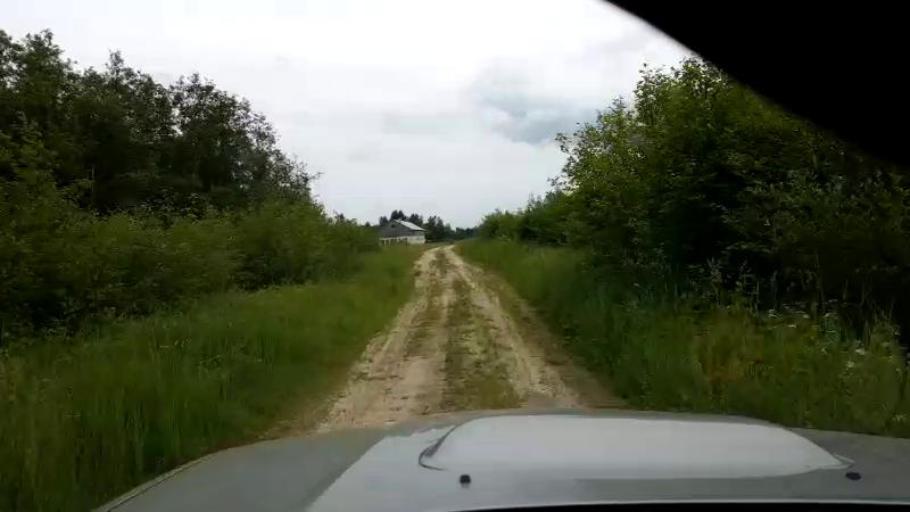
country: EE
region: Paernumaa
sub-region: Halinga vald
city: Parnu-Jaagupi
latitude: 58.5341
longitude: 24.6180
